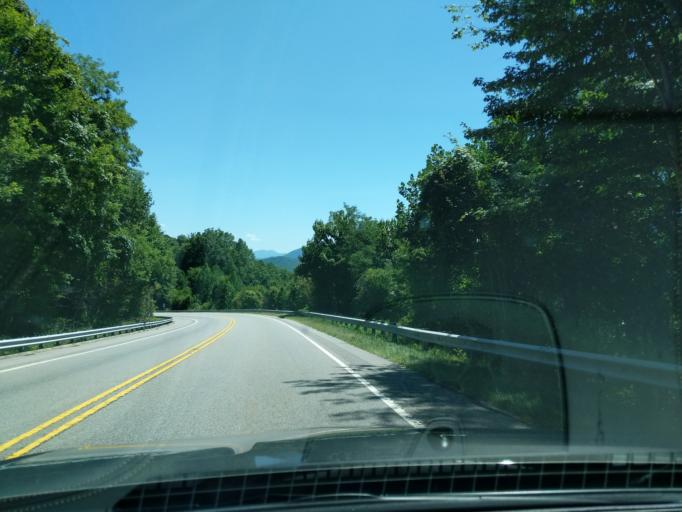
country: US
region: North Carolina
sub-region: Macon County
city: Franklin
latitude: 35.1295
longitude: -83.5252
